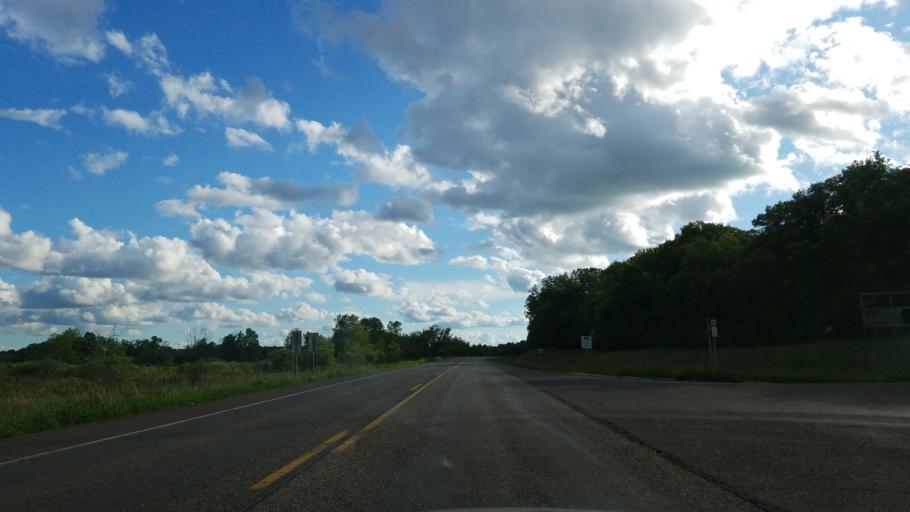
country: US
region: Wisconsin
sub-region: Polk County
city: Osceola
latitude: 45.3369
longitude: -92.6816
